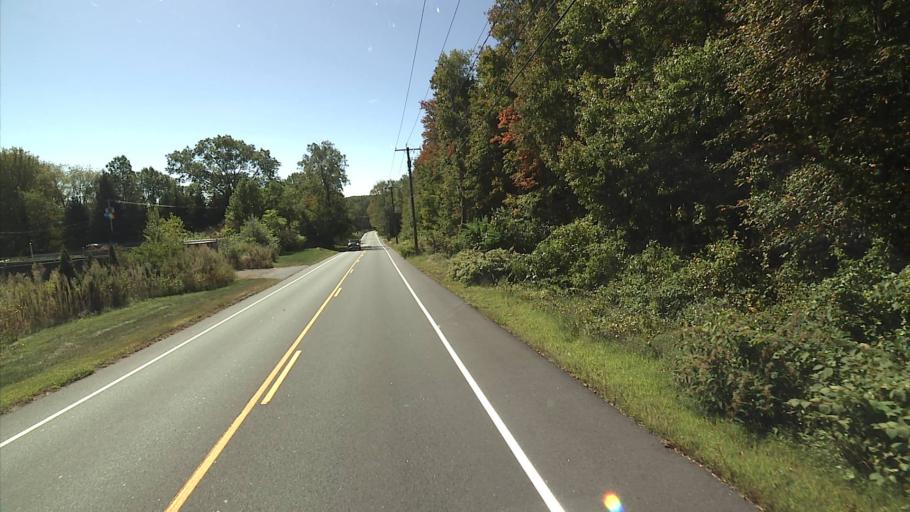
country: US
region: Connecticut
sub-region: New Haven County
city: Prospect
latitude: 41.4654
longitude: -72.9662
